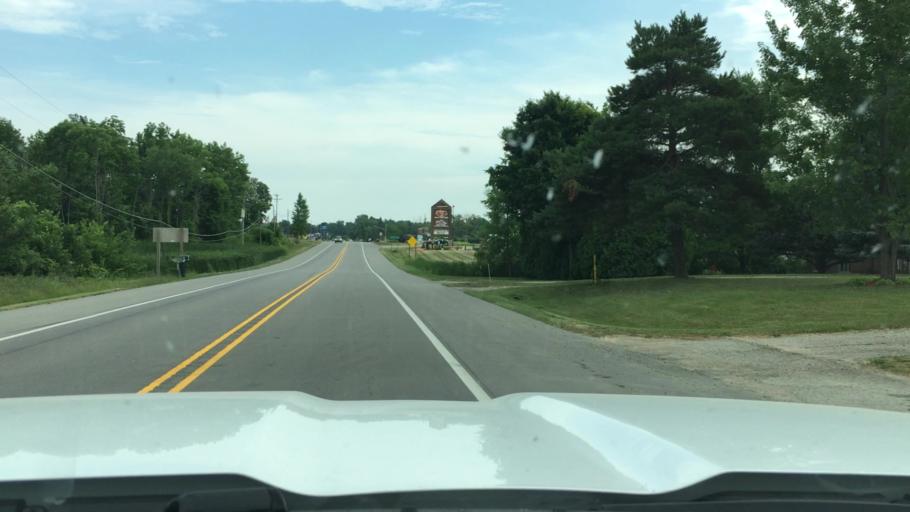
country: US
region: Michigan
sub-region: Sanilac County
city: Marlette
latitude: 43.3459
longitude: -83.0847
